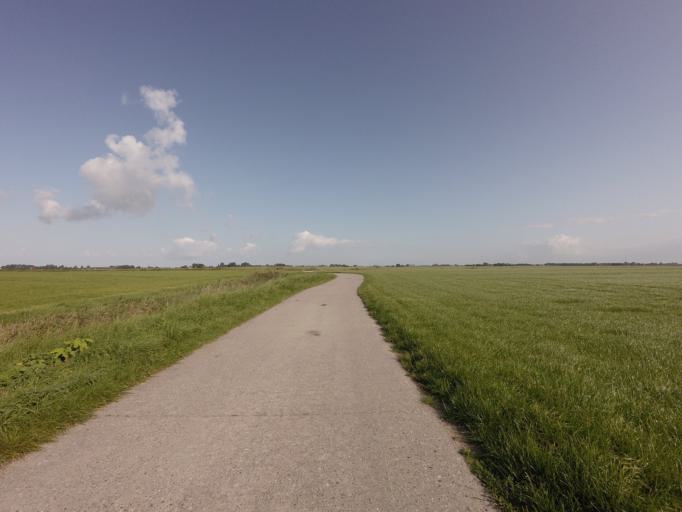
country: NL
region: Friesland
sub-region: Gemeente Franekeradeel
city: Franeker
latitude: 53.2028
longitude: 5.5768
